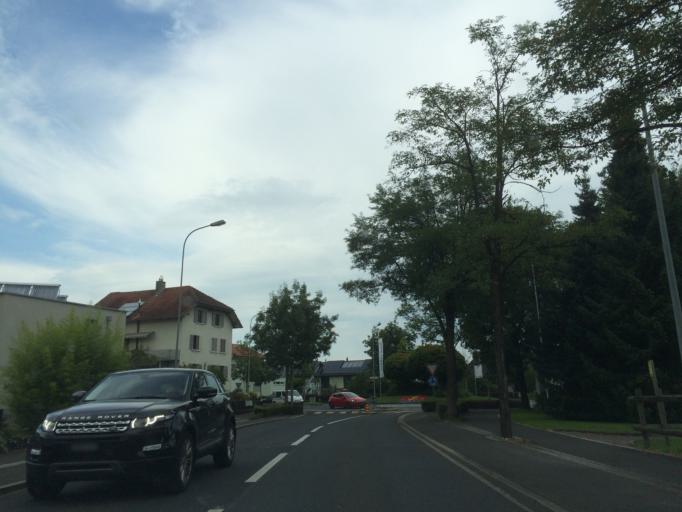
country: LI
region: Ruggell
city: Ruggell
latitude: 47.2412
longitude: 9.5247
